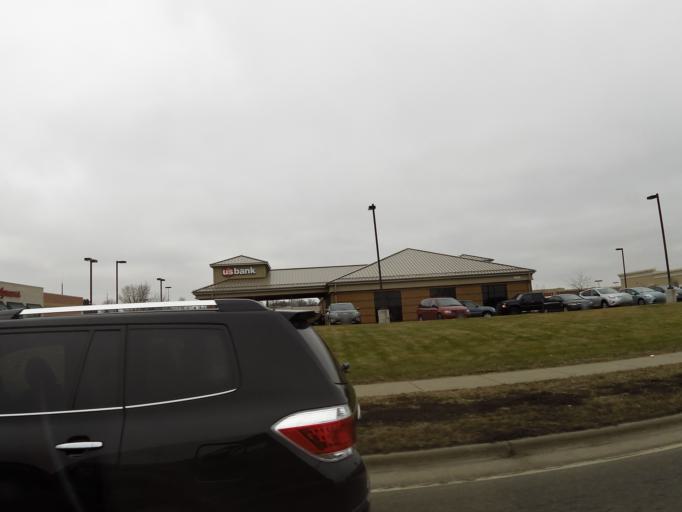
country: US
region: Minnesota
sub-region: Dakota County
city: Burnsville
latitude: 44.7466
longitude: -93.2911
